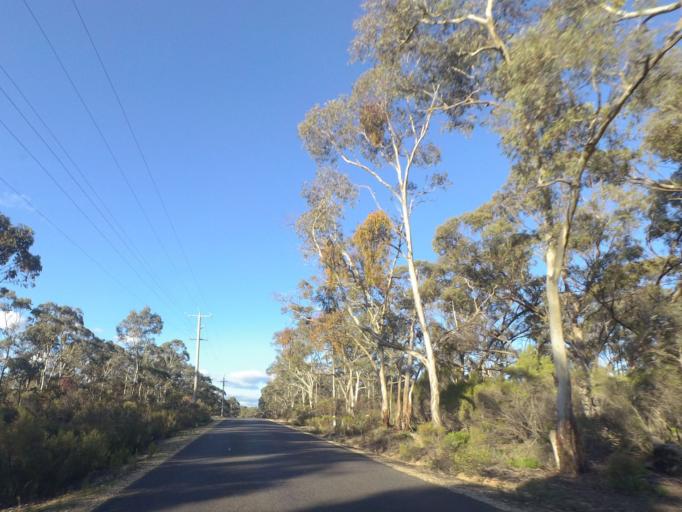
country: AU
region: Victoria
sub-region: Mount Alexander
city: Castlemaine
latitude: -37.1431
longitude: 144.1917
